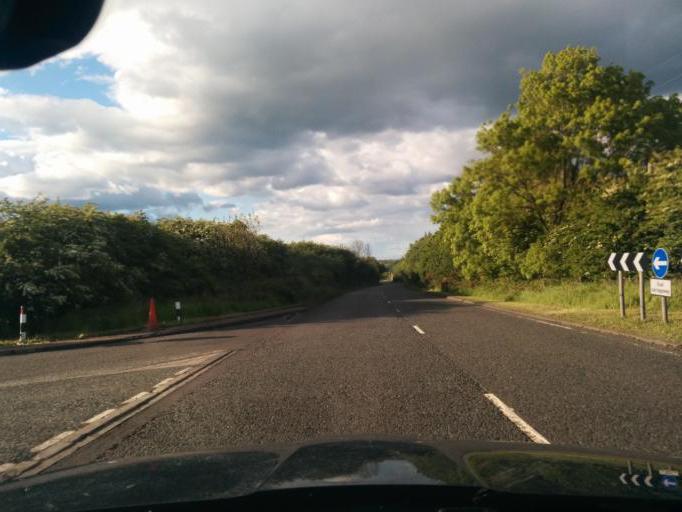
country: GB
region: England
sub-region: Northumberland
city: Cramlington
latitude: 55.0922
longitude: -1.6196
